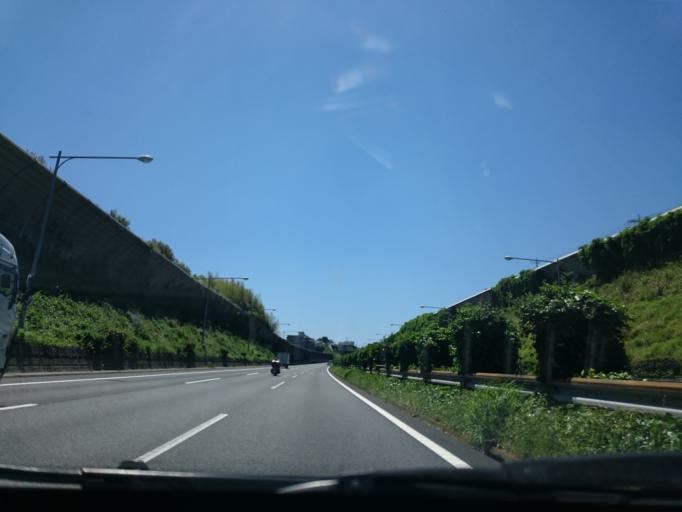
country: JP
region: Kanagawa
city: Hadano
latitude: 35.3700
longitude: 139.2622
